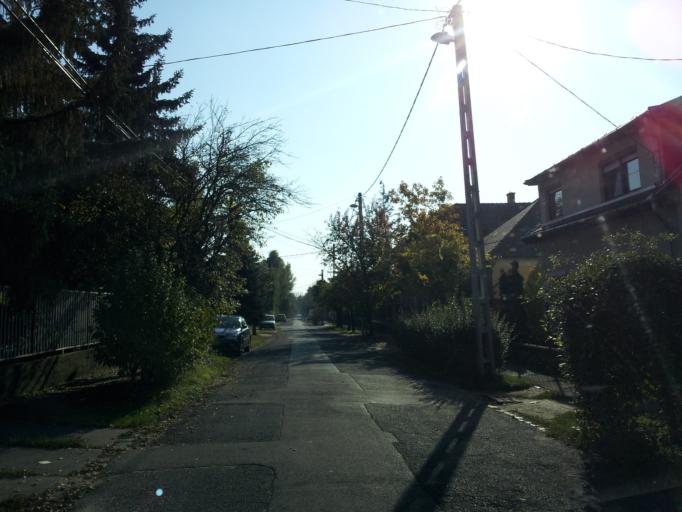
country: HU
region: Budapest
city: Budapest XVIII. keruelet
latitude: 47.4612
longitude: 19.1865
